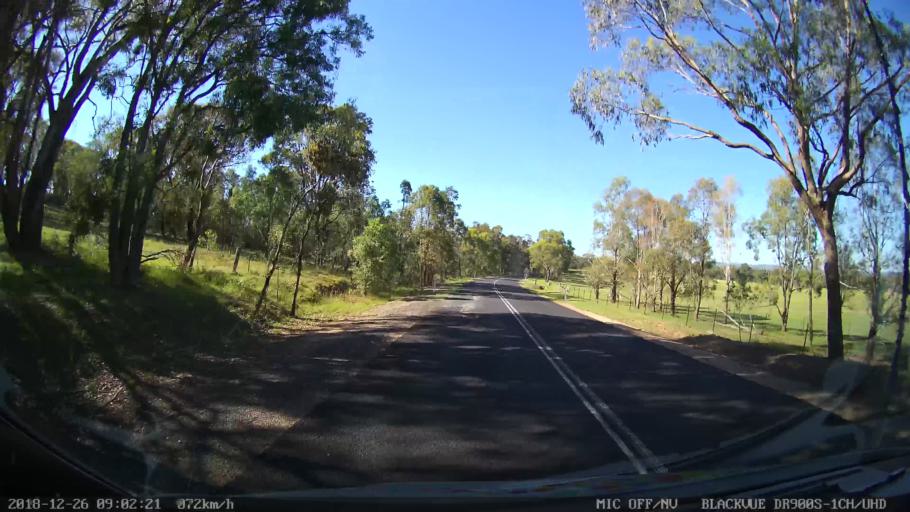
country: AU
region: New South Wales
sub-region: Mid-Western Regional
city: Kandos
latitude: -32.6518
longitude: 150.0193
